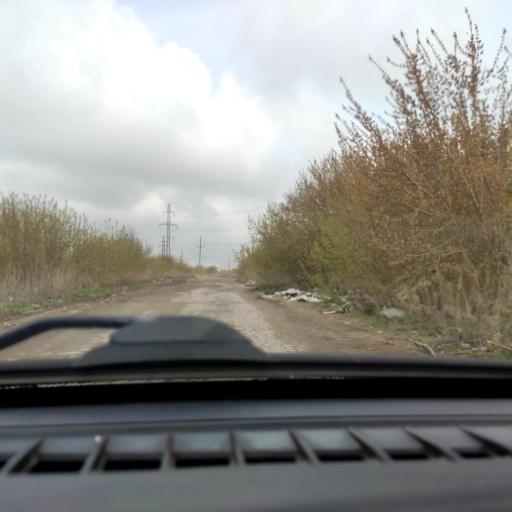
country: RU
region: Samara
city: Zhigulevsk
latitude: 53.5377
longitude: 49.5009
